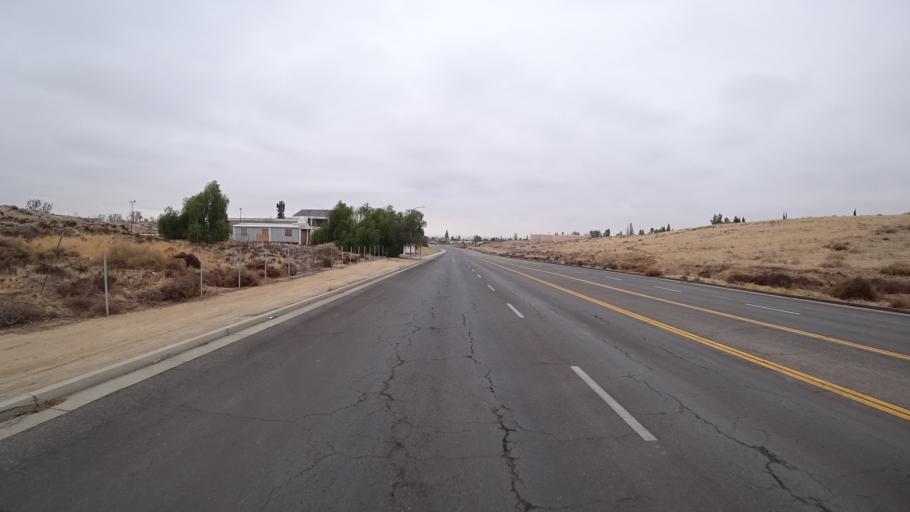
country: US
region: California
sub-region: Kern County
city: Bakersfield
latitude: 35.3867
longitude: -118.9293
